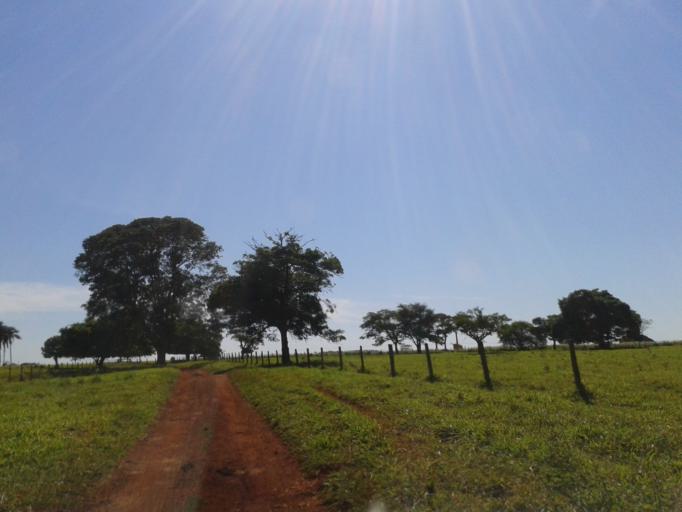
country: BR
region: Minas Gerais
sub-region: Centralina
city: Centralina
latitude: -18.6516
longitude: -49.2966
